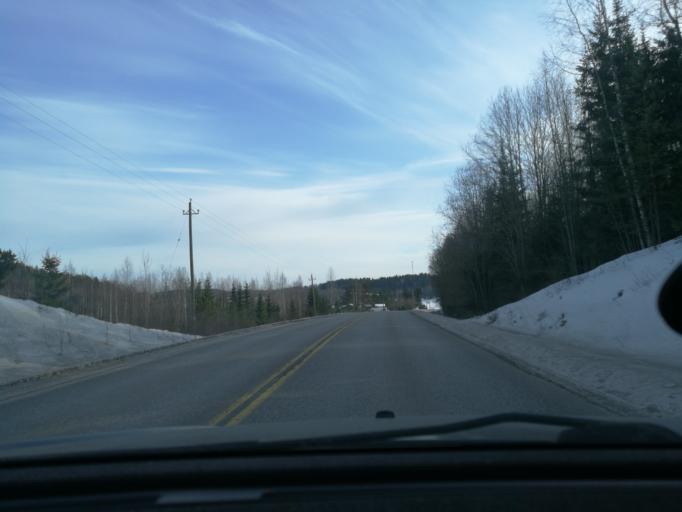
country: FI
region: Uusimaa
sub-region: Helsinki
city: Saukkola
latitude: 60.3960
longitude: 24.0717
